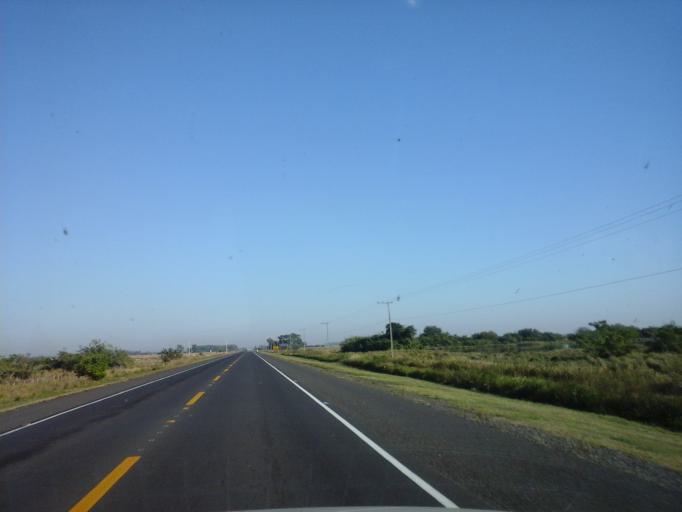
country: PY
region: Neembucu
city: Pilar
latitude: -26.8501
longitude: -58.2278
